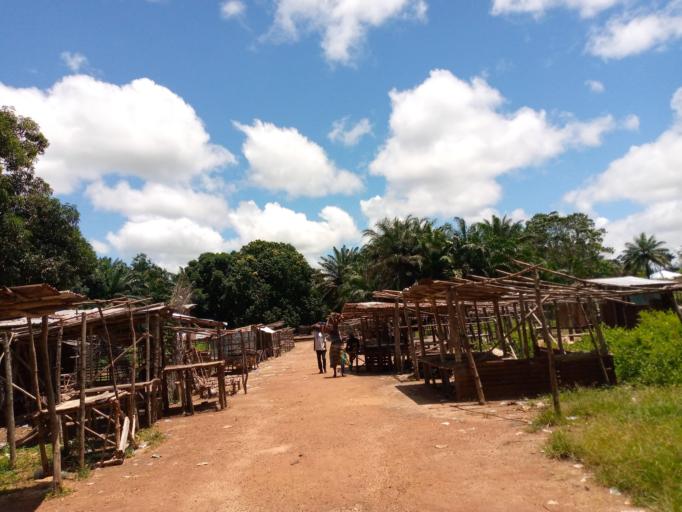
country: SL
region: Northern Province
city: Makeni
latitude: 9.0313
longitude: -12.1601
